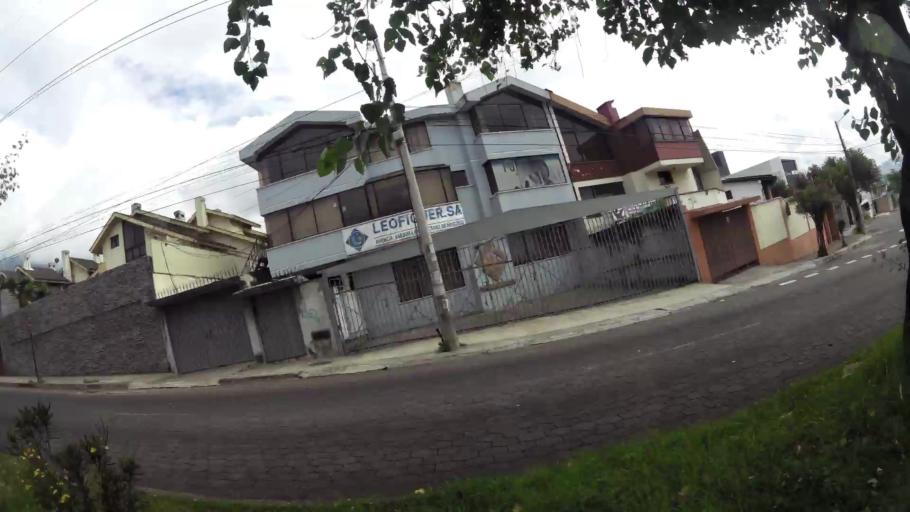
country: EC
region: Pichincha
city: Quito
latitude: -0.1601
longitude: -78.4926
